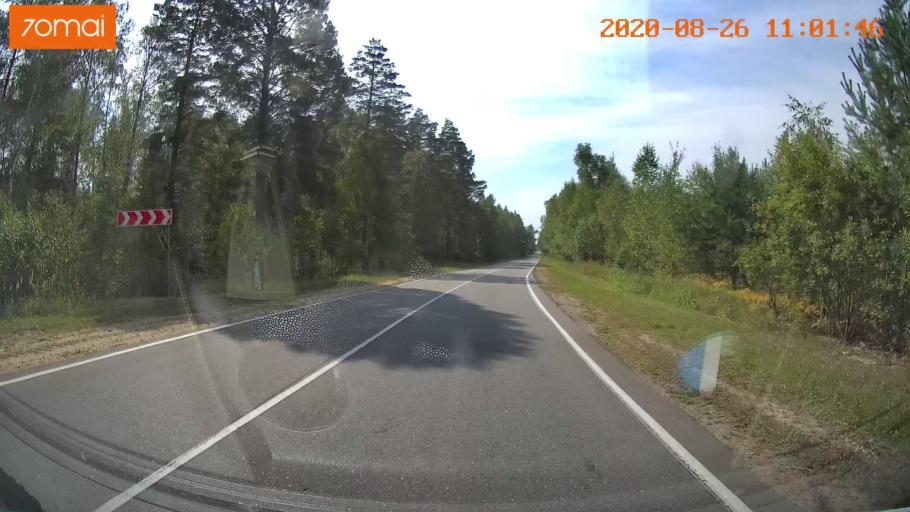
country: RU
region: Rjazan
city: Izhevskoye
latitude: 54.5593
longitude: 41.2275
